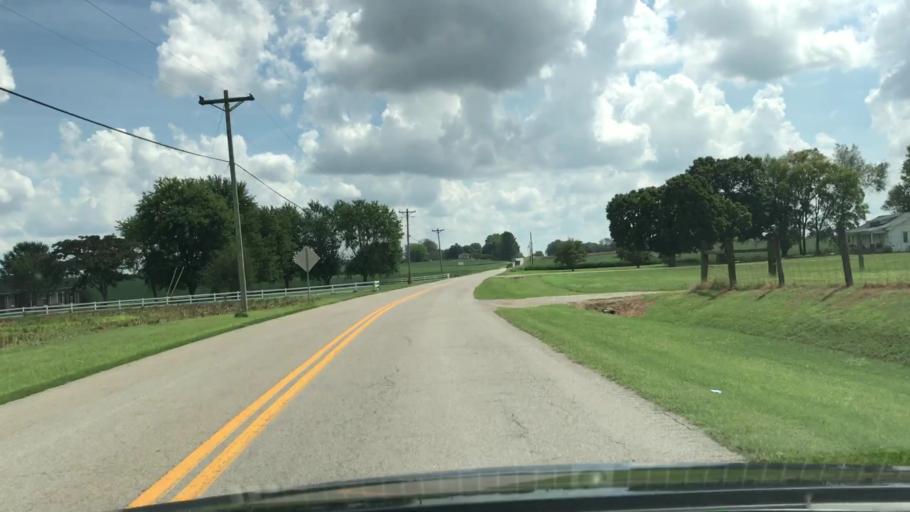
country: US
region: Kentucky
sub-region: Todd County
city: Guthrie
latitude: 36.7139
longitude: -87.0626
